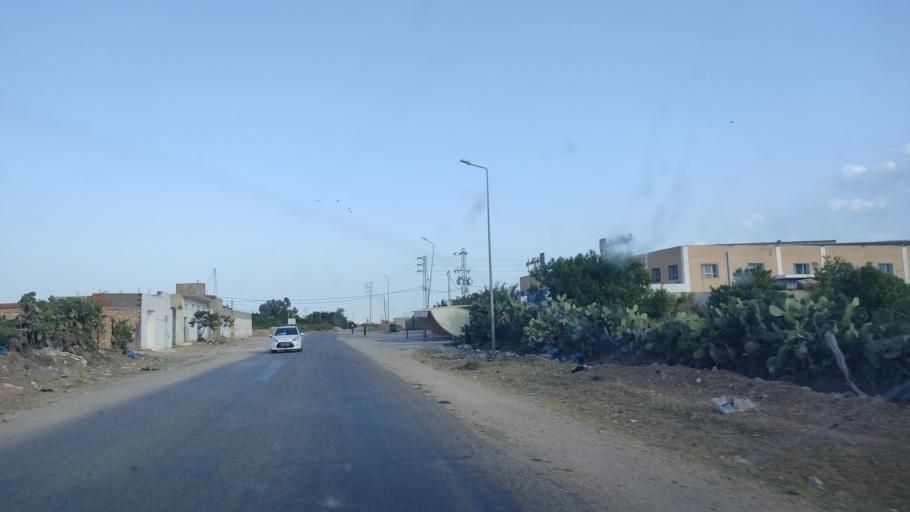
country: TN
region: Safaqis
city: Sfax
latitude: 34.8100
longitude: 10.6634
